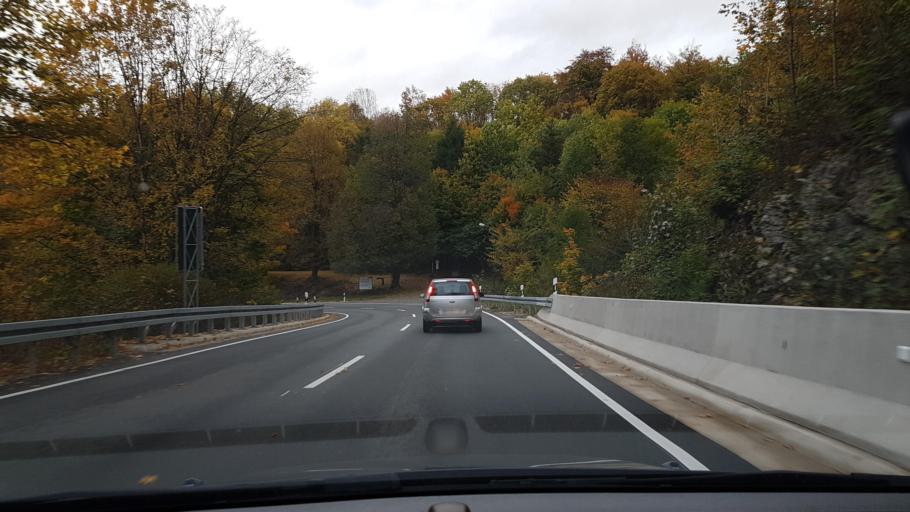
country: DE
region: Lower Saxony
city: Bad Grund
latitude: 51.8227
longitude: 10.2322
